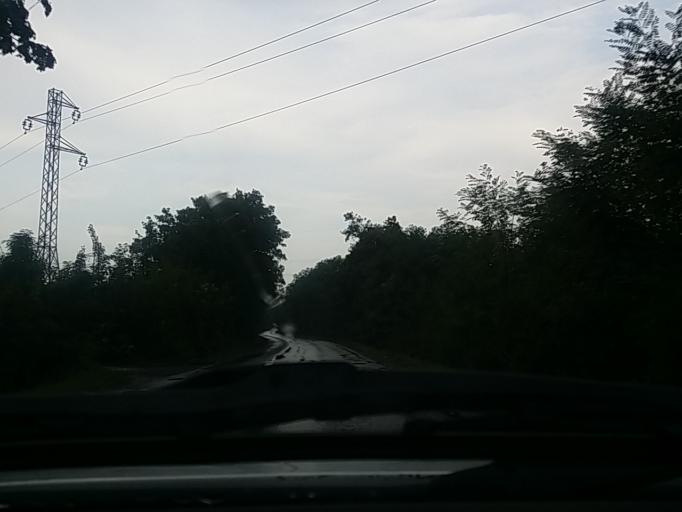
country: HU
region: Pest
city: Budakeszi
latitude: 47.5053
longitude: 18.9095
